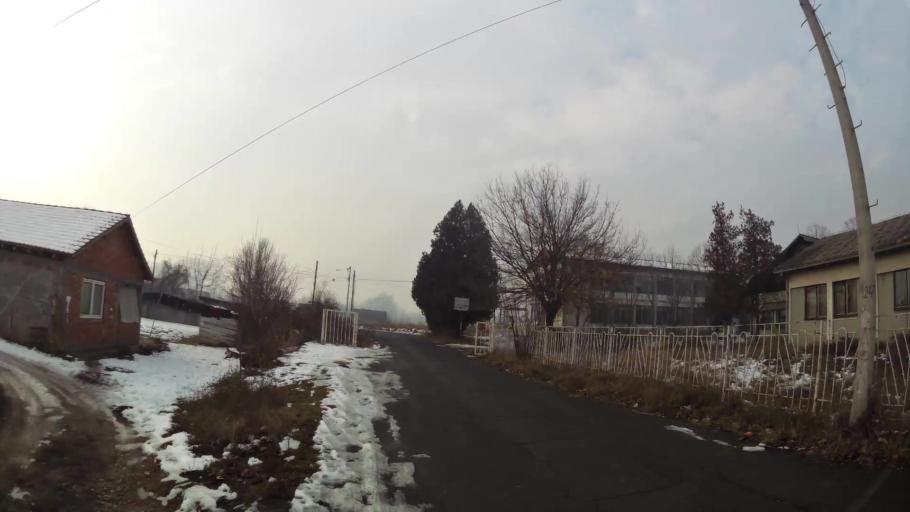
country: MK
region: Ilinden
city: Jurumleri
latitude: 41.9774
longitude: 21.5308
